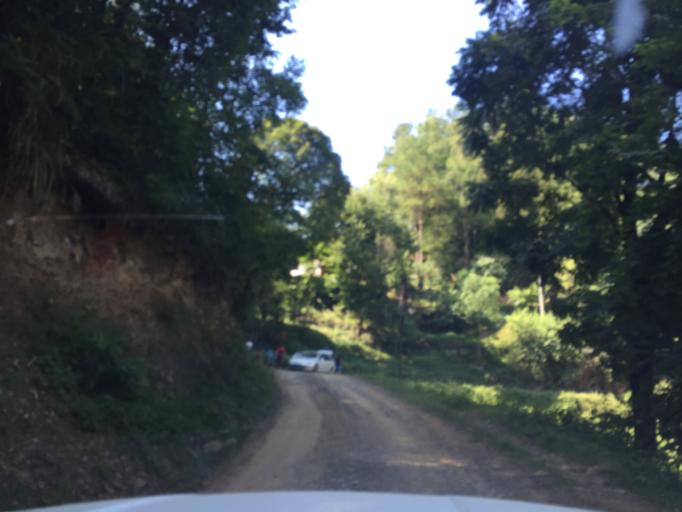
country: CN
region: Guizhou Sheng
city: Jiashi
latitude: 28.3338
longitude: 108.3020
